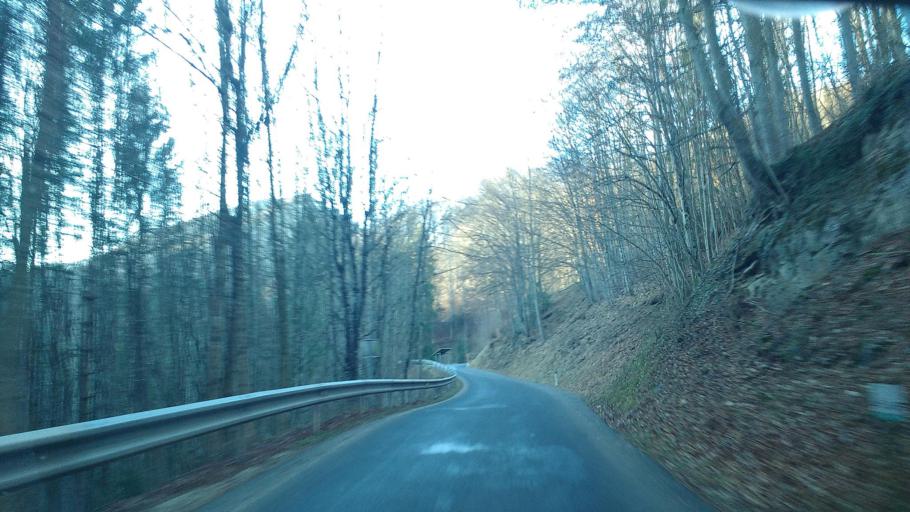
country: AT
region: Upper Austria
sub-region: Politischer Bezirk Kirchdorf an der Krems
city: Gruenburg
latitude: 47.8943
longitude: 14.2216
